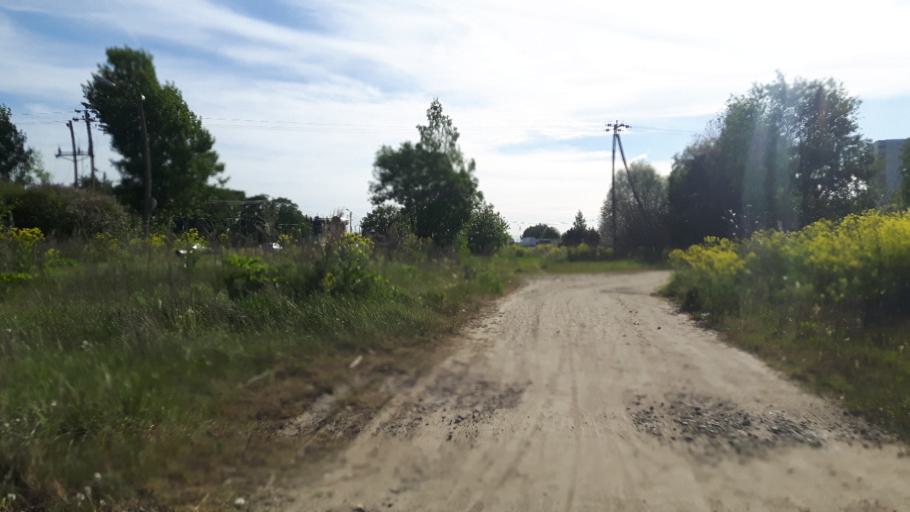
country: EE
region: Harju
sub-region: Tallinna linn
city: Kose
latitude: 59.4438
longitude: 24.9089
